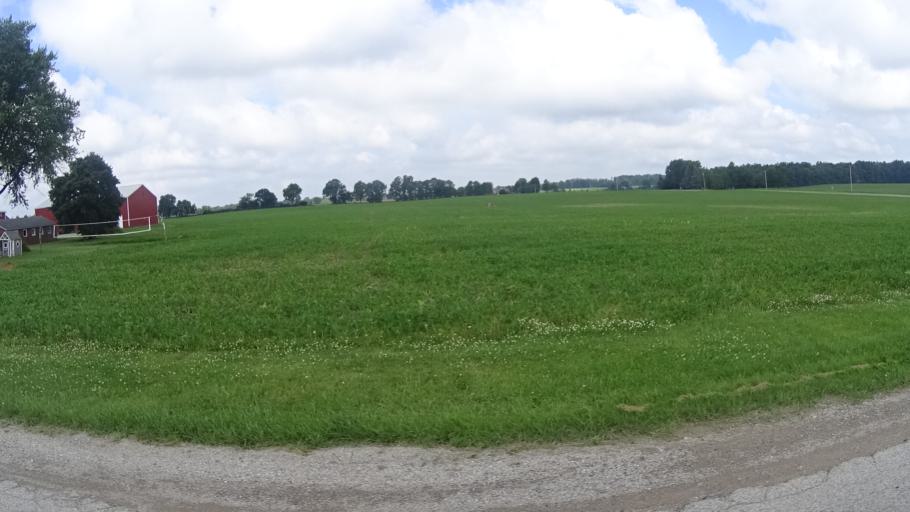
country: US
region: Ohio
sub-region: Huron County
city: Wakeman
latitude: 41.3043
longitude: -82.3874
